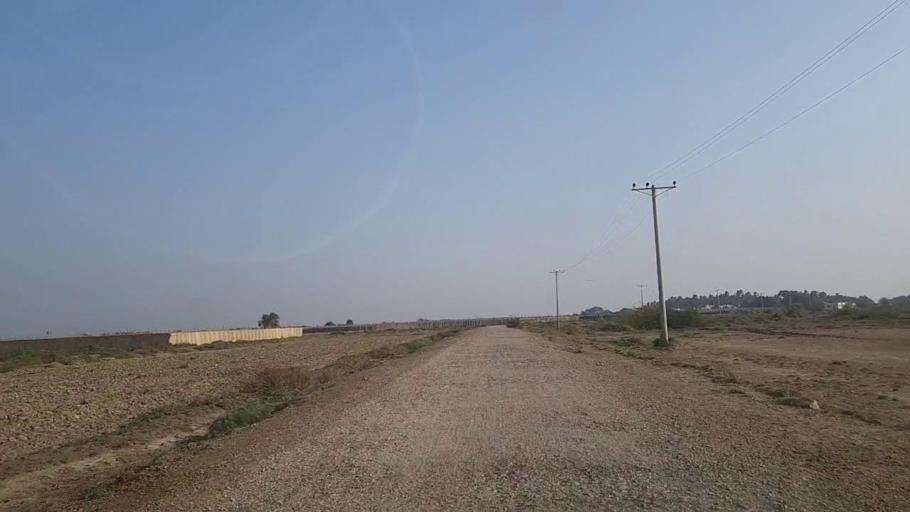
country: PK
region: Sindh
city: Keti Bandar
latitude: 24.1699
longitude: 67.6250
